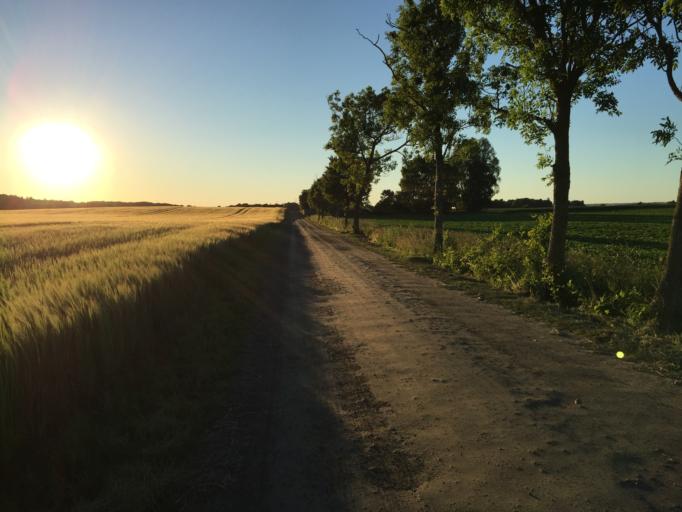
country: SE
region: Skane
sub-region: Lunds Kommun
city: Veberod
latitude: 55.6345
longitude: 13.4743
